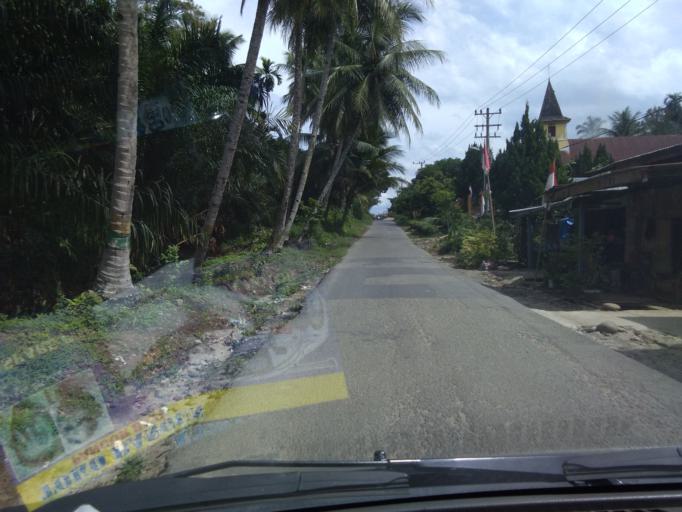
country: ID
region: North Sumatra
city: Deli Tua
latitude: 3.3037
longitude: 98.8082
